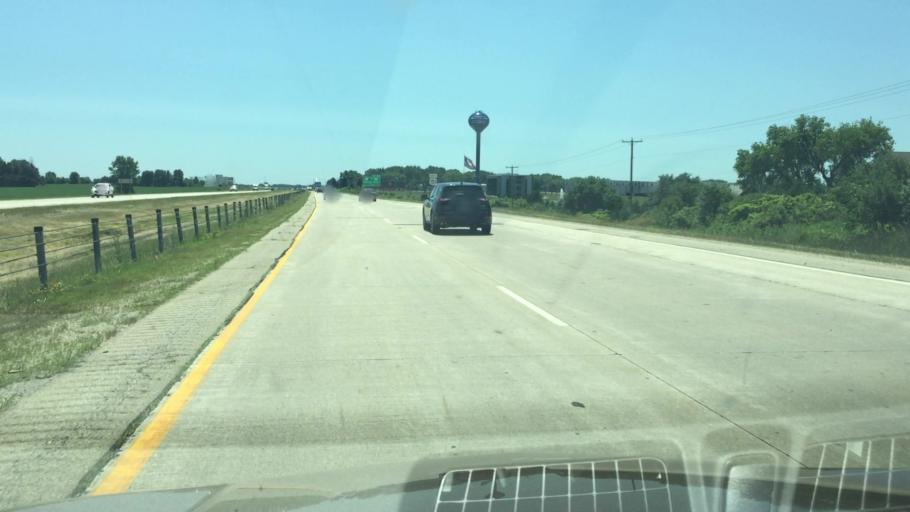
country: US
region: Wisconsin
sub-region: Dodge County
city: Beaver Dam
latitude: 43.5019
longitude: -88.8094
